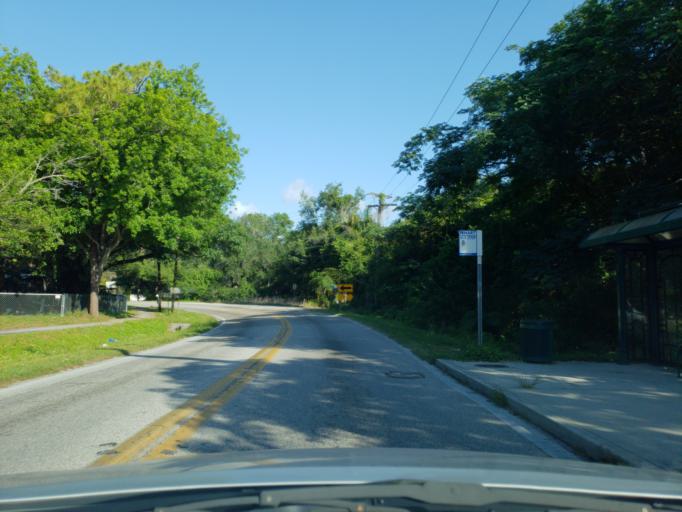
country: US
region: Florida
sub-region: Hillsborough County
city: Palm River-Clair Mel
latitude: 27.9427
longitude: -82.3860
